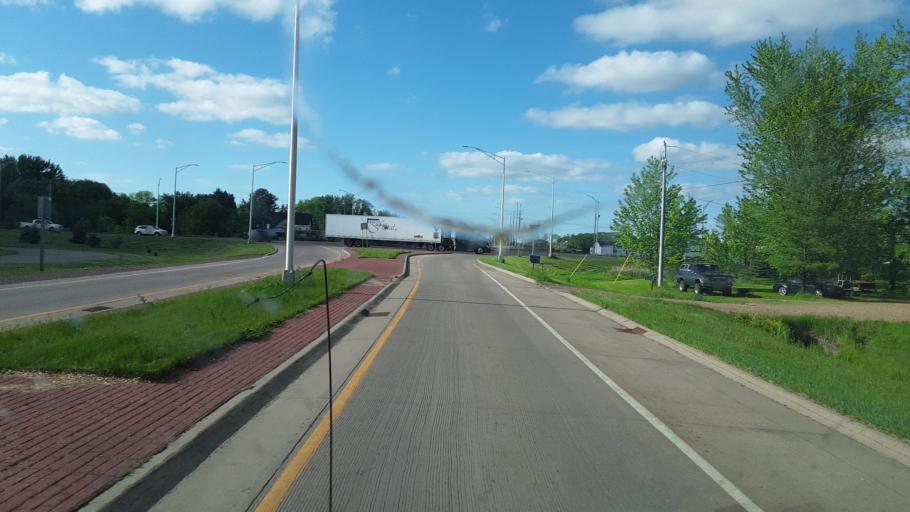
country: US
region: Wisconsin
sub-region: Wood County
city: Marshfield
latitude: 44.5970
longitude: -90.1805
